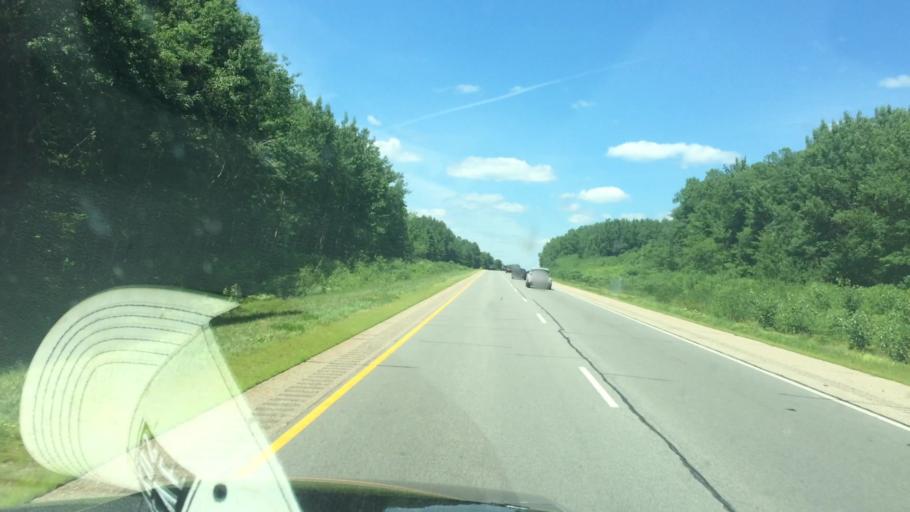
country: US
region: Wisconsin
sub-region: Marathon County
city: Mosinee
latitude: 44.7004
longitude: -89.6494
